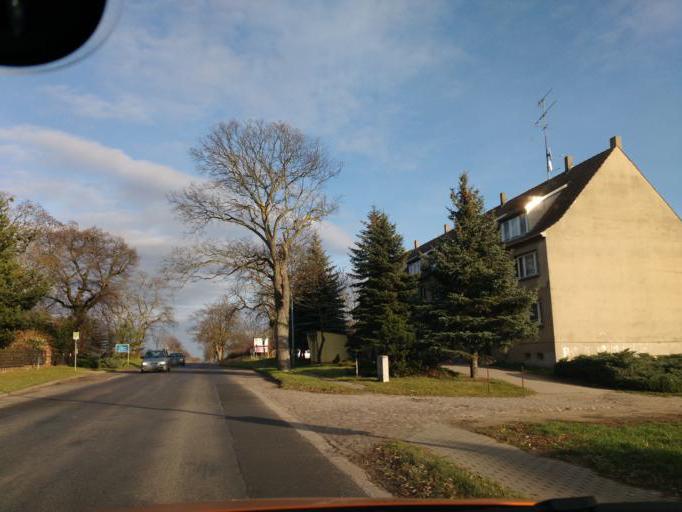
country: DE
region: Brandenburg
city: Wriezen
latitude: 52.6909
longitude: 14.1025
